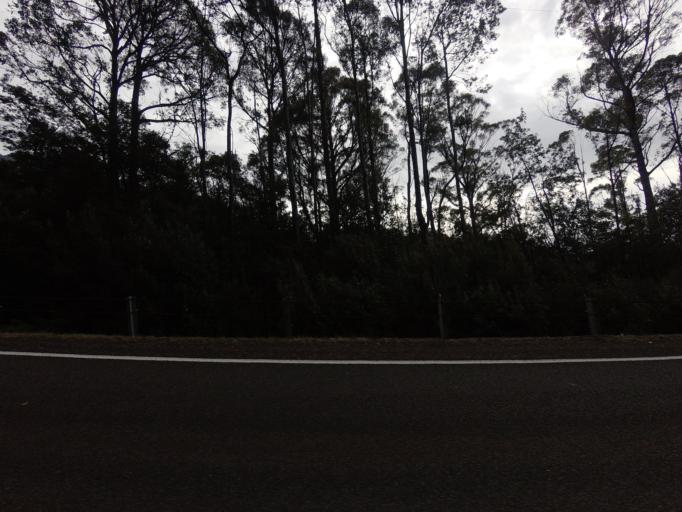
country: AU
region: Tasmania
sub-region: Meander Valley
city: Deloraine
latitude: -41.6487
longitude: 146.7209
